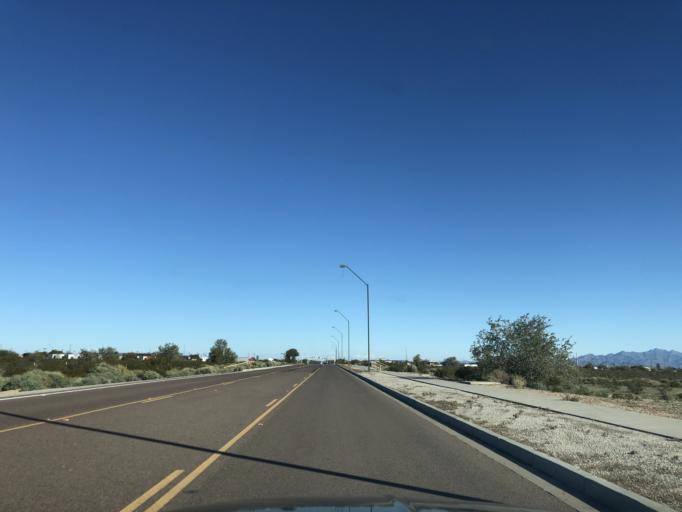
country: US
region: Arizona
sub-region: Maricopa County
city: Buckeye
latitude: 33.4281
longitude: -112.5975
